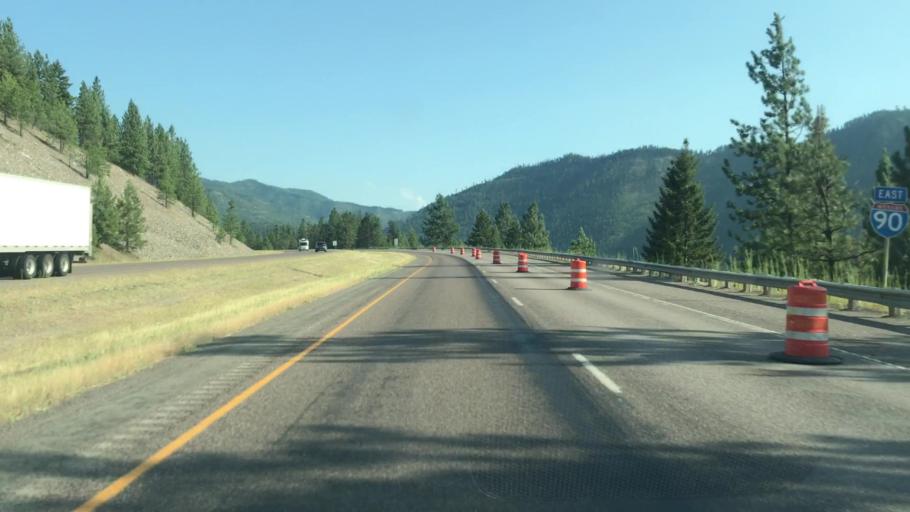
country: US
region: Montana
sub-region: Mineral County
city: Superior
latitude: 47.0197
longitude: -114.7365
